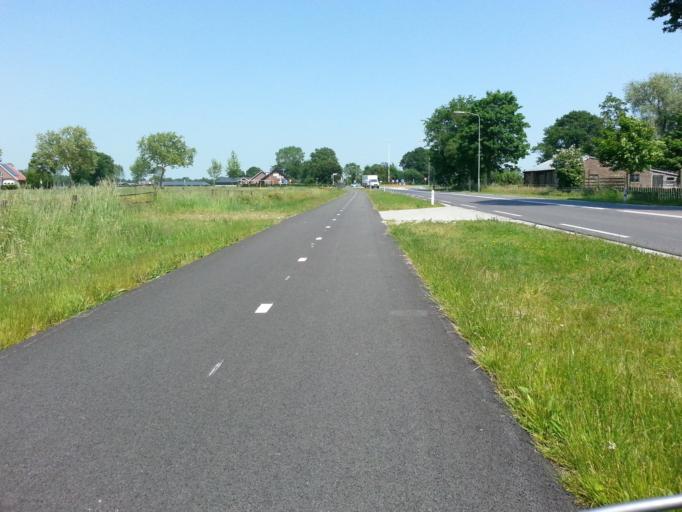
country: NL
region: Gelderland
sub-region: Gemeente Barneveld
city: Barneveld
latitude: 52.1180
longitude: 5.5402
